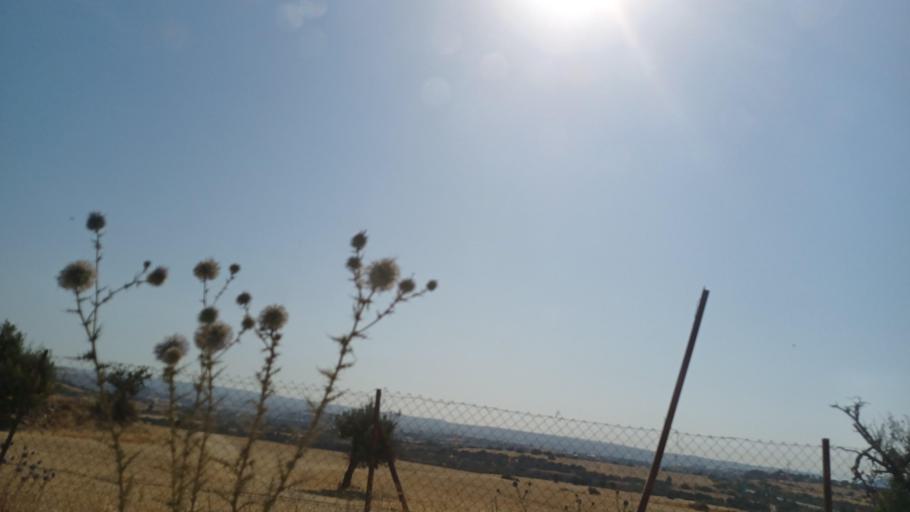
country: CY
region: Limassol
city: Pissouri
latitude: 34.6872
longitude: 32.7403
